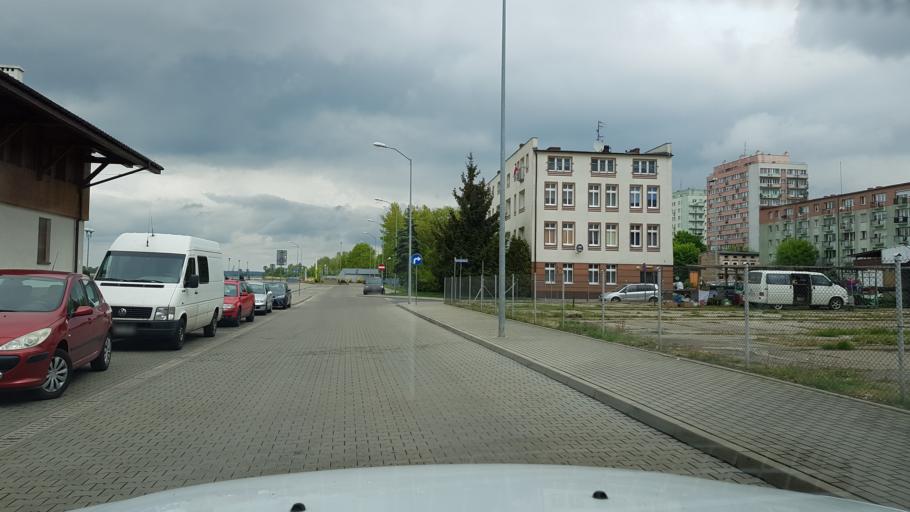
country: PL
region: West Pomeranian Voivodeship
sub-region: Powiat gryfinski
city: Gryfino
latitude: 53.2532
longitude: 14.4840
